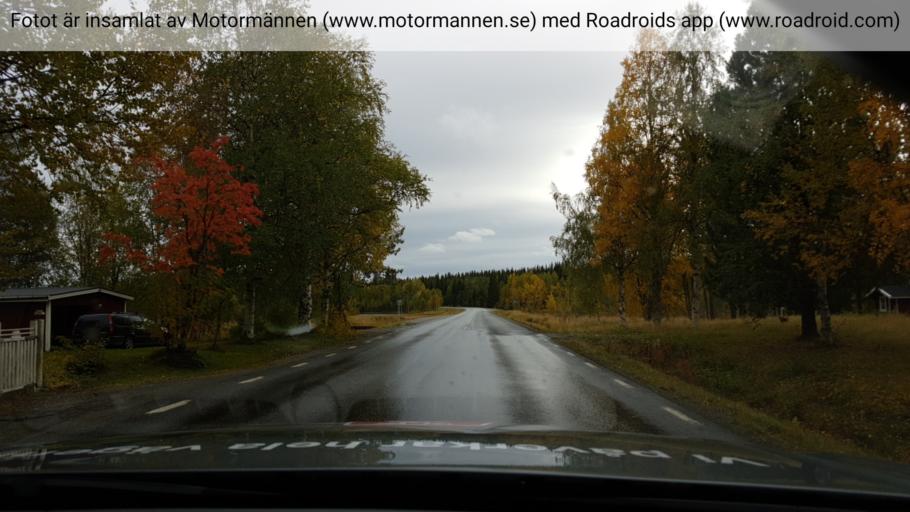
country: SE
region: Vaesterbotten
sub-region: Vilhelmina Kommun
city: Sjoberg
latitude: 64.6756
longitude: 16.2922
